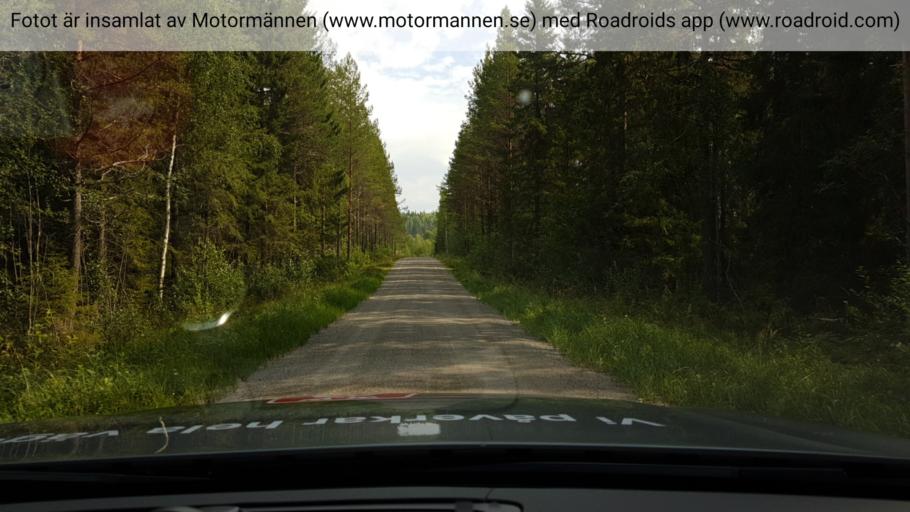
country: SE
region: Jaemtland
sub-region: OEstersunds Kommun
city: Brunflo
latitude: 63.0344
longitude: 15.0754
